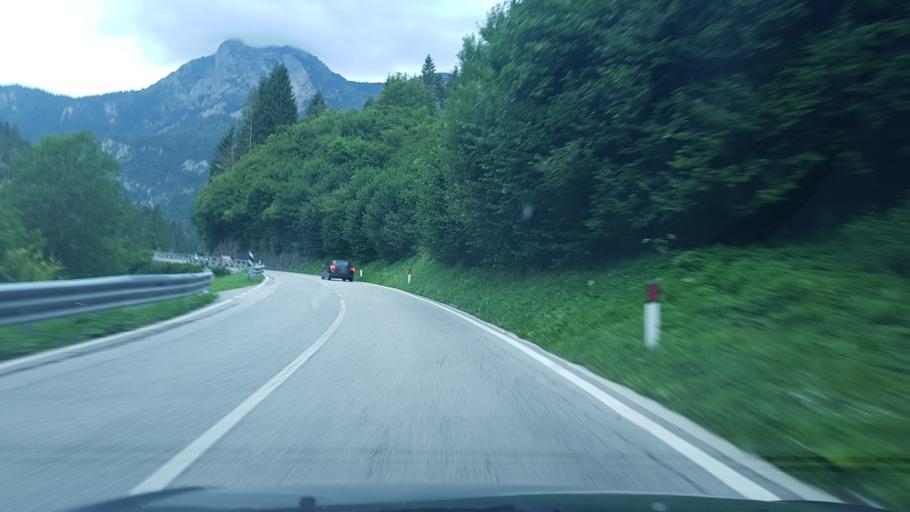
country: IT
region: Friuli Venezia Giulia
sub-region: Provincia di Udine
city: Forni Avoltri
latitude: 46.5792
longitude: 12.7902
